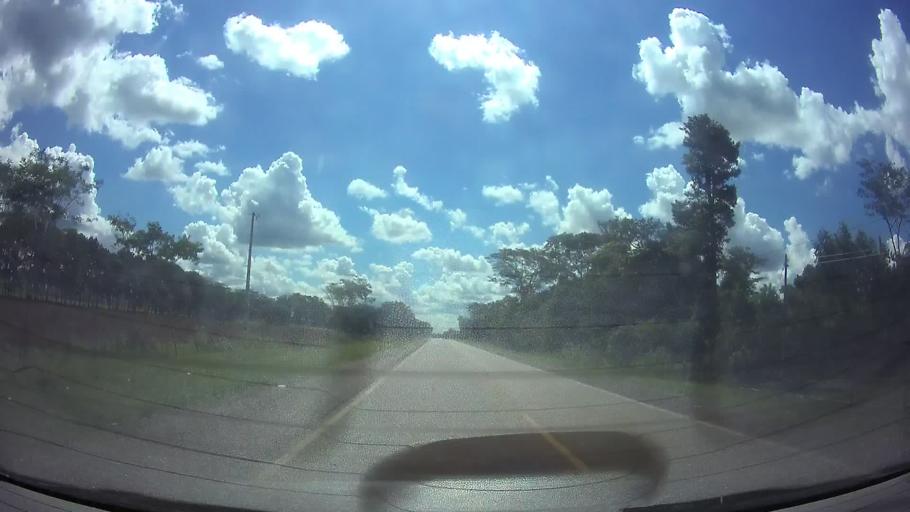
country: PY
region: Paraguari
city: La Colmena
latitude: -25.9048
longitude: -56.7692
